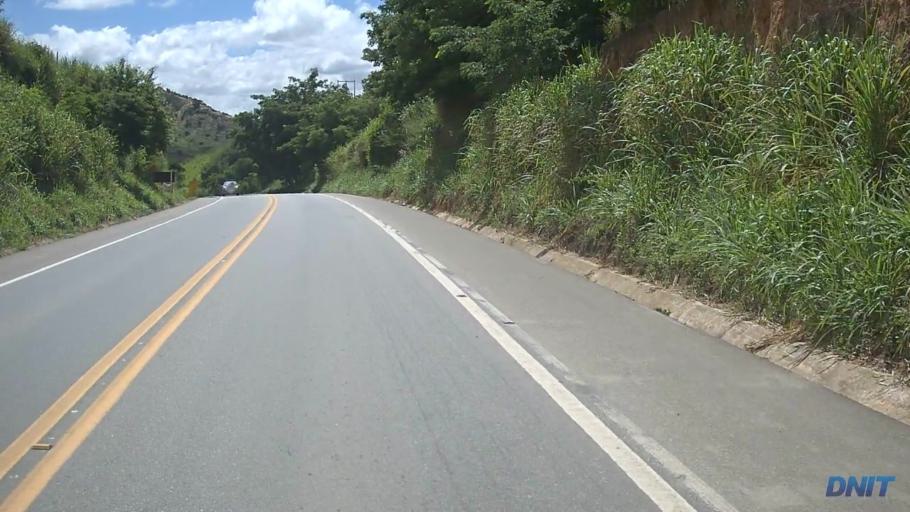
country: BR
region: Minas Gerais
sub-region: Governador Valadares
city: Governador Valadares
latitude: -18.9549
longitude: -42.0737
